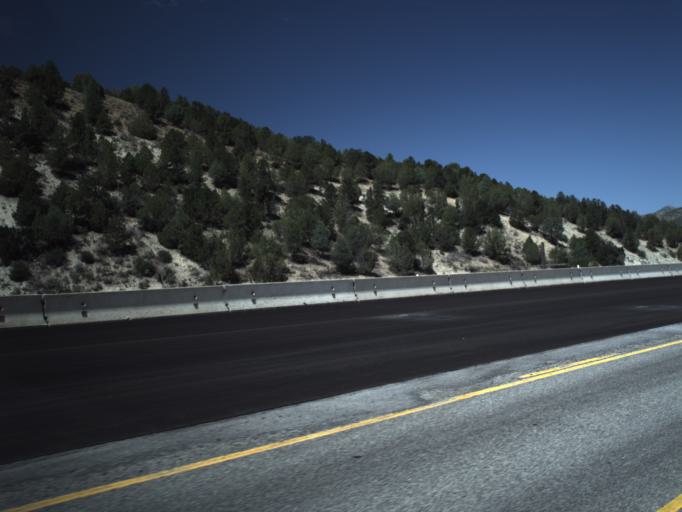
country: US
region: Utah
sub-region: Utah County
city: Mapleton
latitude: 39.9587
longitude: -111.3028
